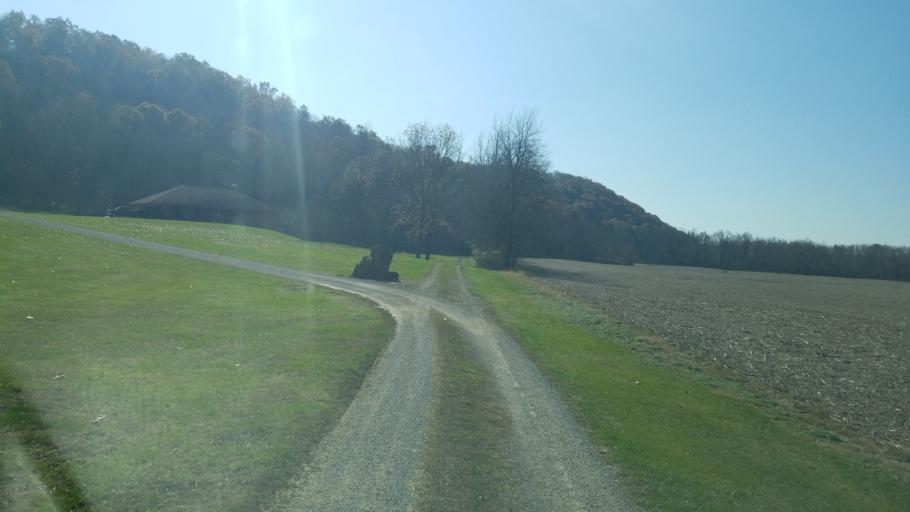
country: US
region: Ohio
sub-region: Licking County
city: Newark
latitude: 40.1300
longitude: -82.4188
